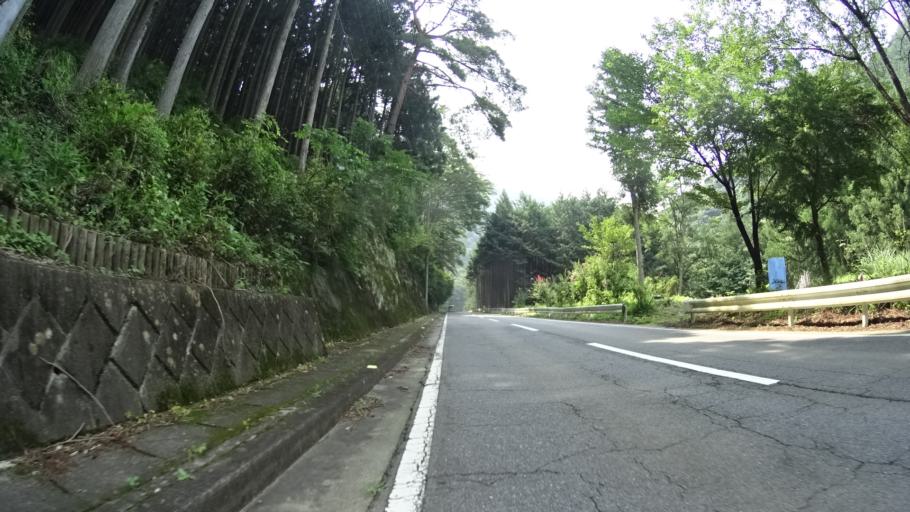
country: JP
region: Gunma
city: Tomioka
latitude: 36.0873
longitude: 138.8018
